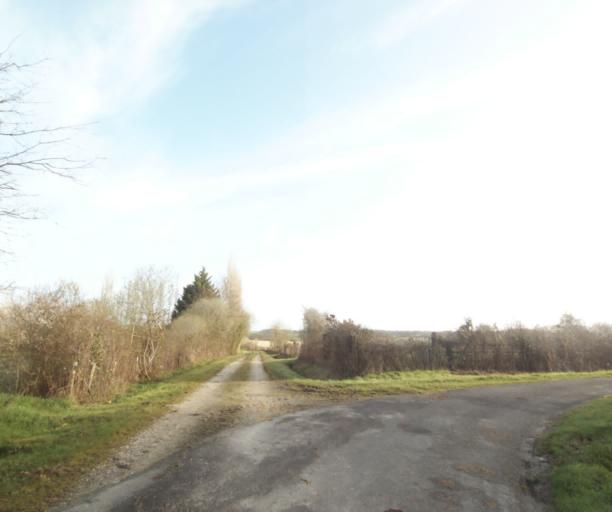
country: FR
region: Pays de la Loire
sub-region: Departement de la Loire-Atlantique
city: Savenay
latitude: 47.3874
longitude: -1.9034
